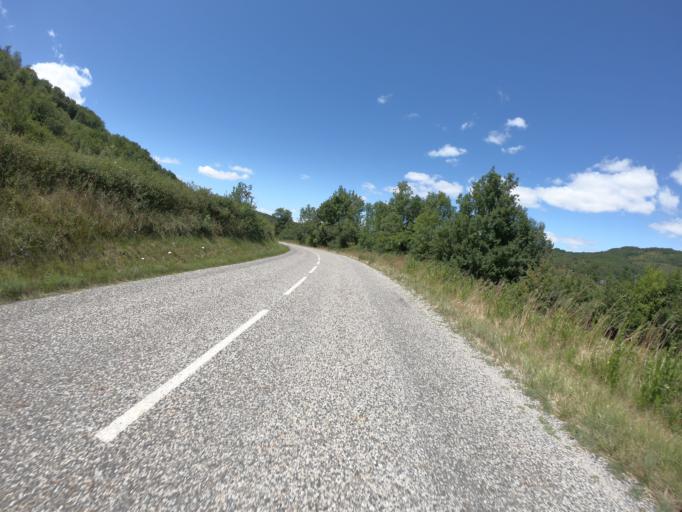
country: FR
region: Midi-Pyrenees
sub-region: Departement de l'Ariege
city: Mirepoix
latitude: 43.0439
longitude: 1.7708
